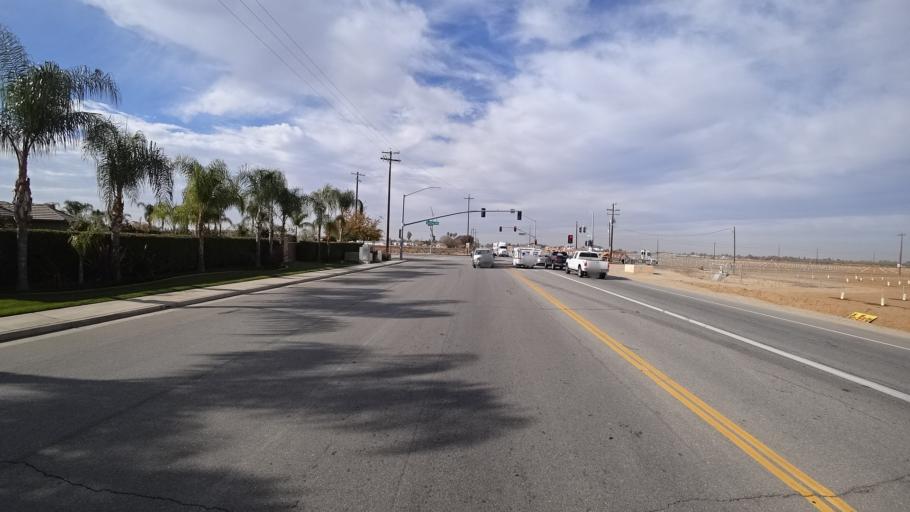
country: US
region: California
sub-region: Kern County
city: Greenacres
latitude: 35.4269
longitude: -119.0915
